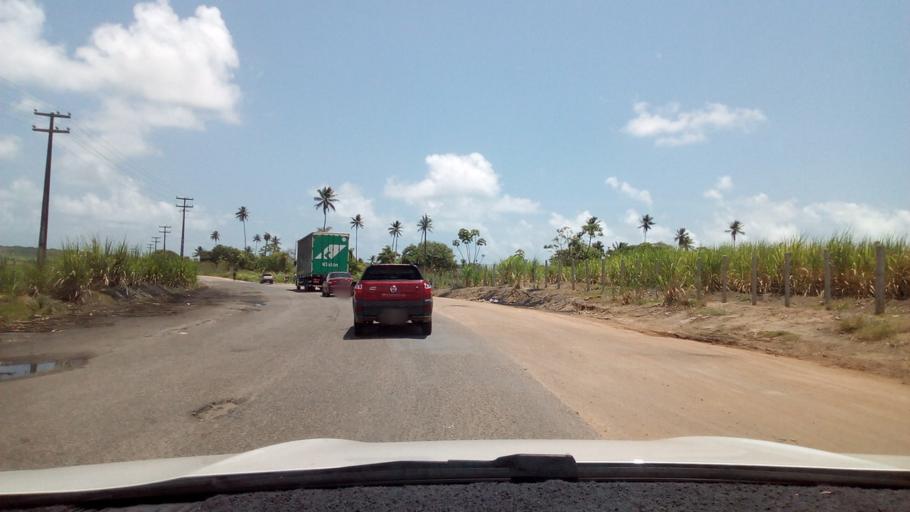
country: BR
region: Paraiba
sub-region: Caapora
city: Caapora
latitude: -7.5178
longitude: -34.8668
